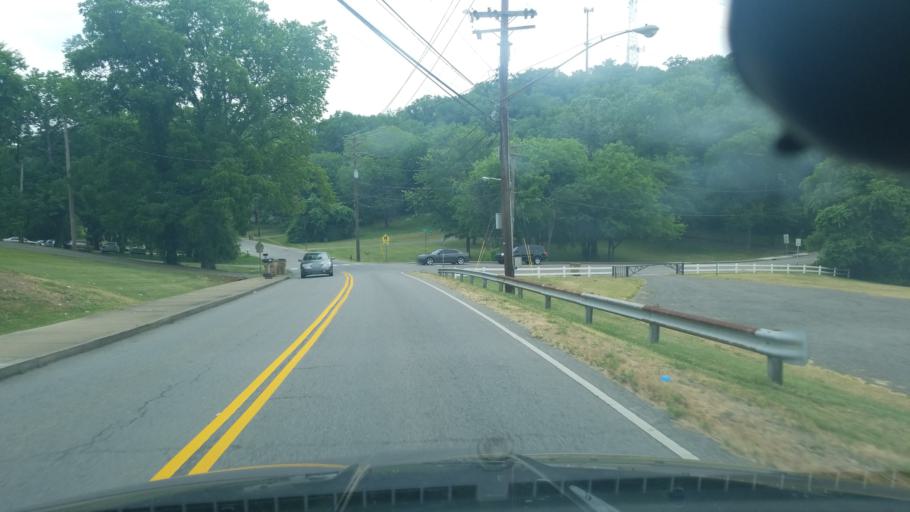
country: US
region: Tennessee
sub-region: Davidson County
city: Goodlettsville
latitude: 36.2534
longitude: -86.7438
